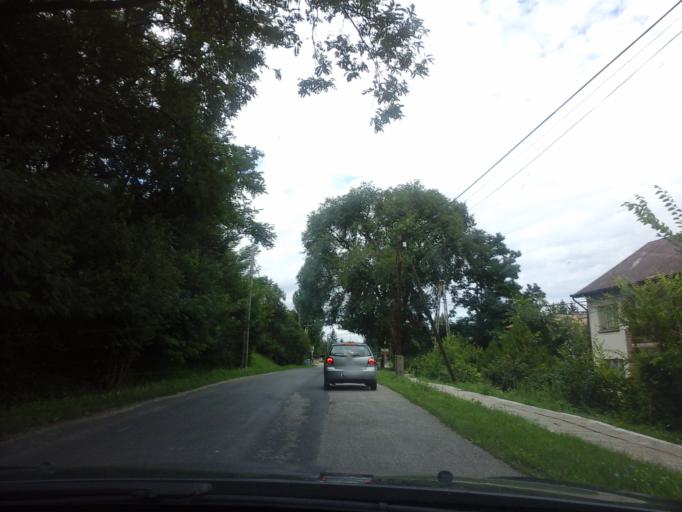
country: HU
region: Borsod-Abauj-Zemplen
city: Izsofalva
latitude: 48.3078
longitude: 20.6255
